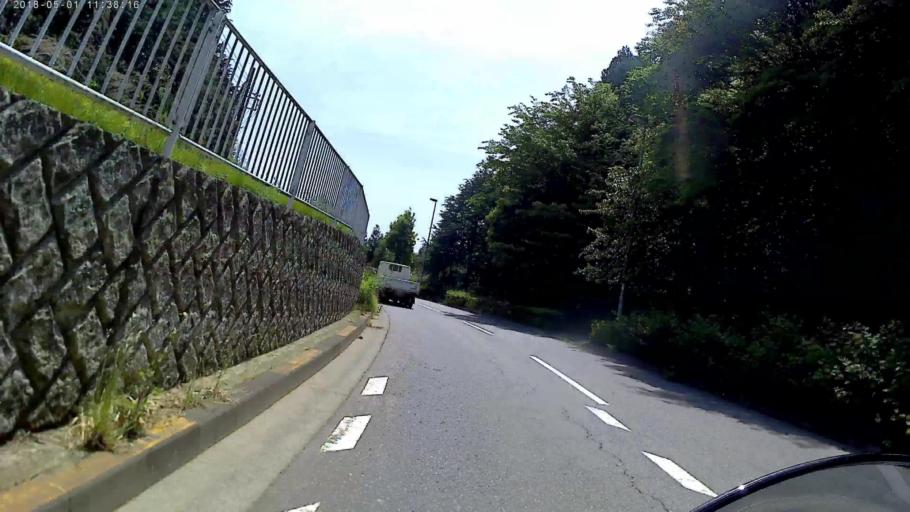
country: JP
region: Kanagawa
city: Minami-rinkan
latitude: 35.5095
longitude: 139.4905
